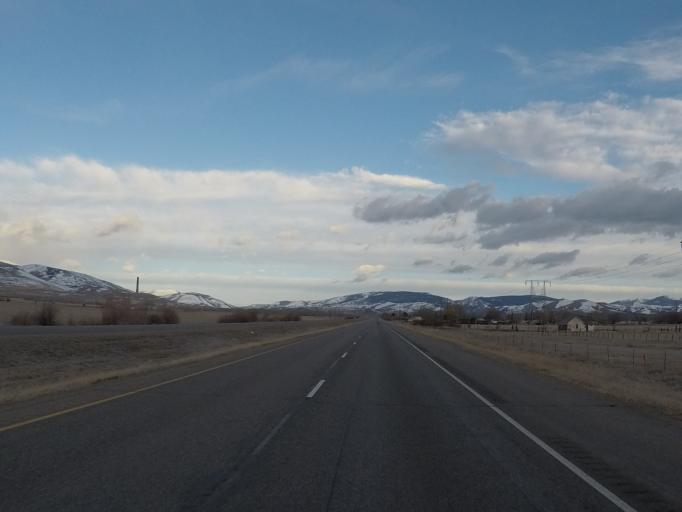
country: US
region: Montana
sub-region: Deer Lodge County
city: Warm Springs
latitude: 46.0983
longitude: -112.8298
